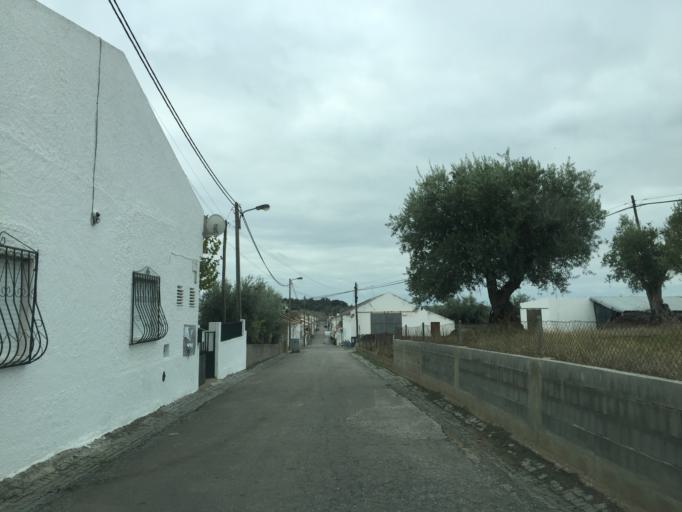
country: PT
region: Portalegre
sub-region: Fronteira
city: Vale da Amoreira
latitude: 39.0478
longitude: -7.7627
